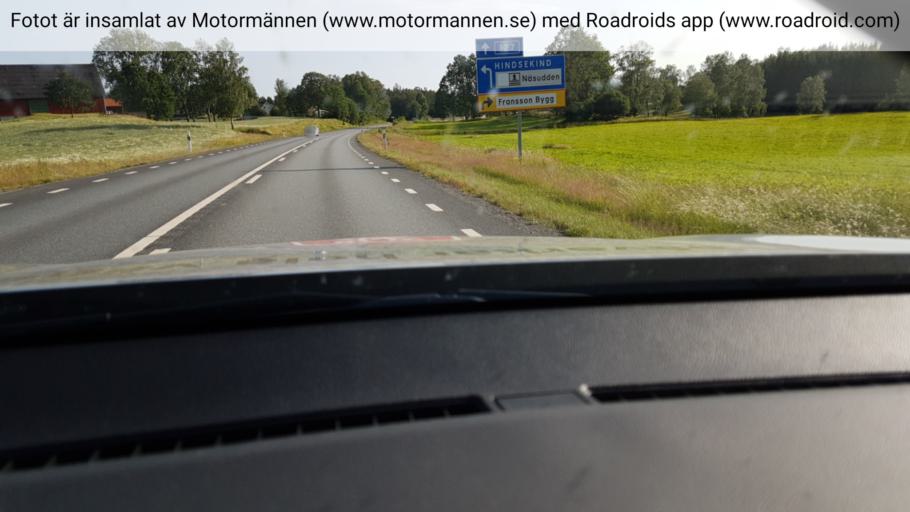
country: SE
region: Joenkoeping
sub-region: Varnamo Kommun
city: Varnamo
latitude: 57.2061
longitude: 14.1008
